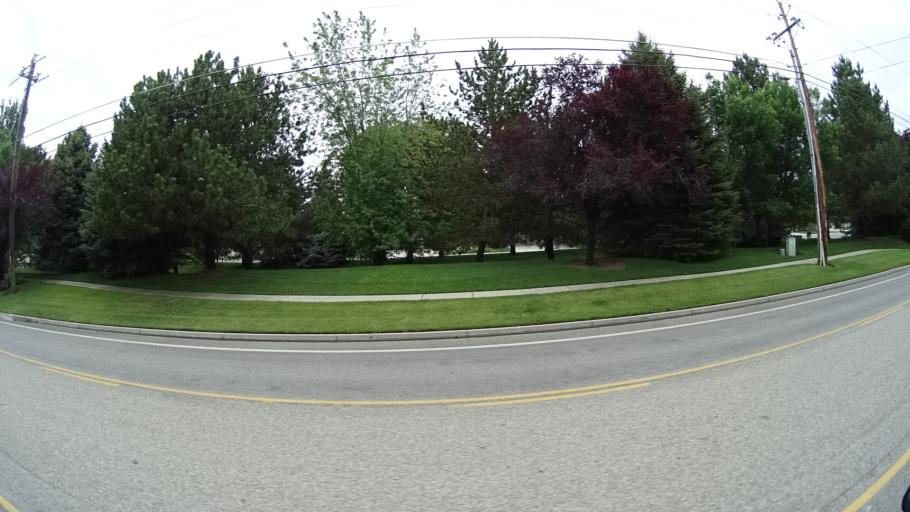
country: US
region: Idaho
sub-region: Ada County
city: Eagle
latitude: 43.7065
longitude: -116.3215
